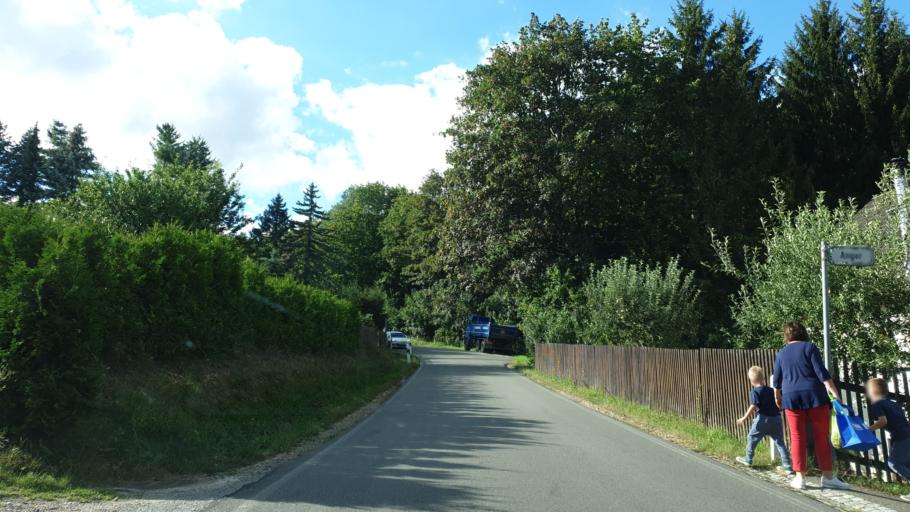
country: DE
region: Saxony
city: Lichtenstein
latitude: 50.7125
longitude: 12.6430
